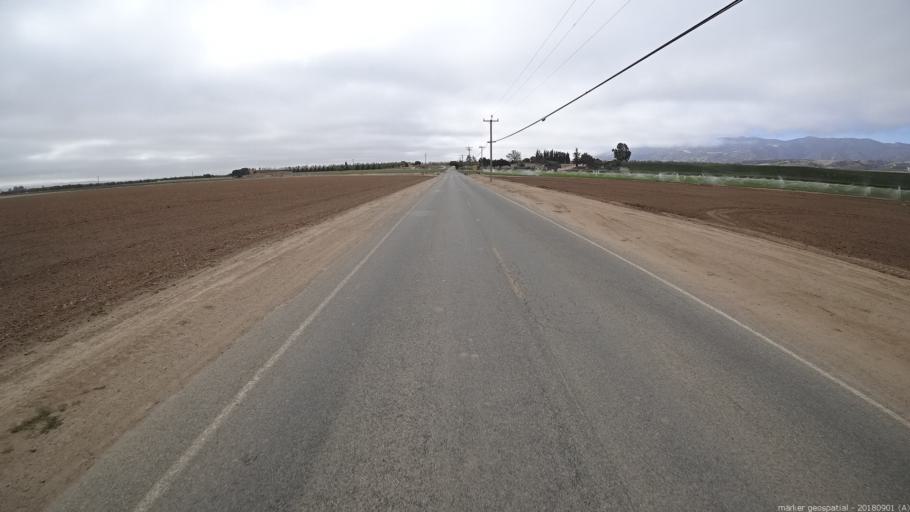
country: US
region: California
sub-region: Monterey County
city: Soledad
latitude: 36.3770
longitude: -121.3274
